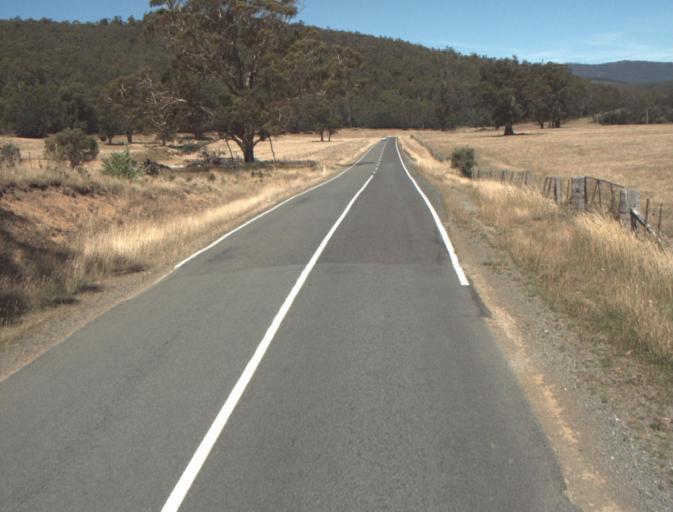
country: AU
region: Tasmania
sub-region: Dorset
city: Scottsdale
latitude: -41.2885
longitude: 147.3845
